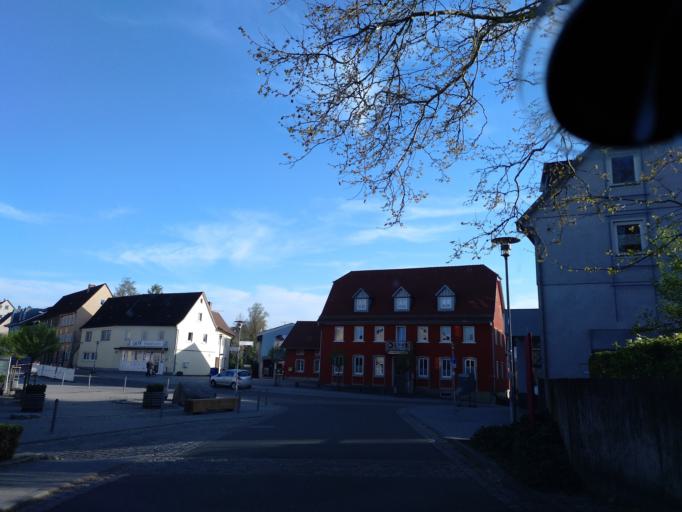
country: DE
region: Baden-Wuerttemberg
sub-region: Regierungsbezirk Stuttgart
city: Kirchberg an der Jagst
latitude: 49.2030
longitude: 9.9808
